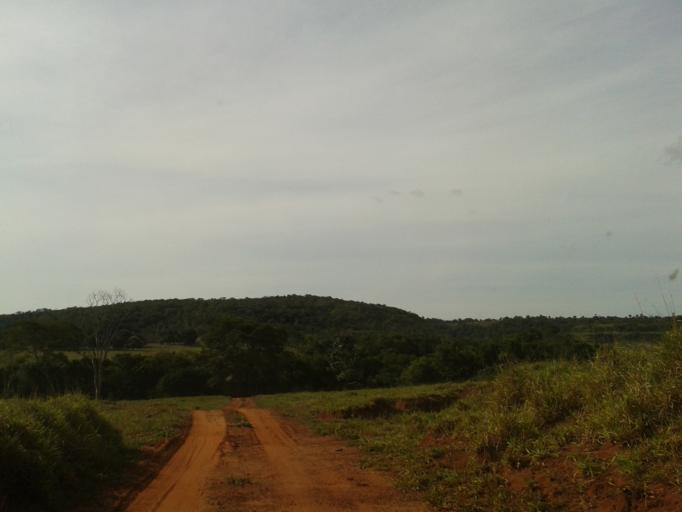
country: BR
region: Minas Gerais
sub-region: Campina Verde
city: Campina Verde
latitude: -19.4989
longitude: -49.5774
